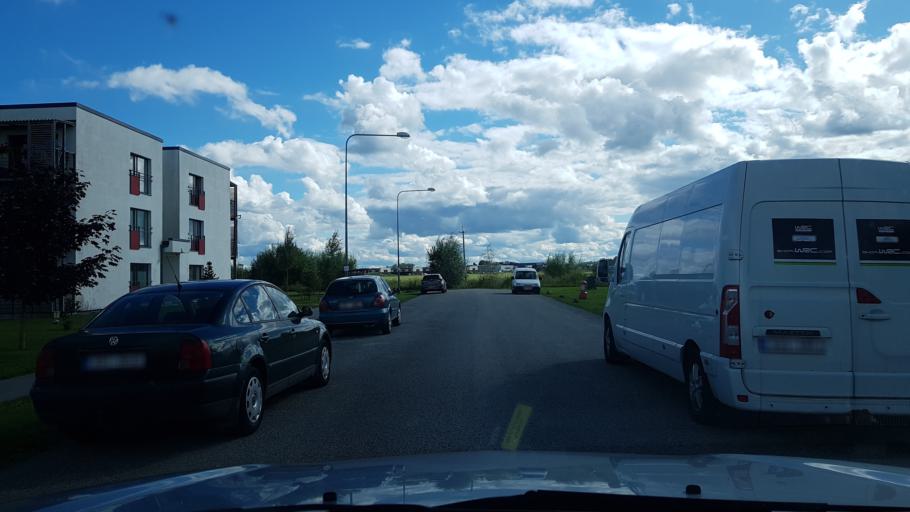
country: EE
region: Harju
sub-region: Tallinna linn
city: Tallinn
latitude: 59.3904
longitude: 24.8112
